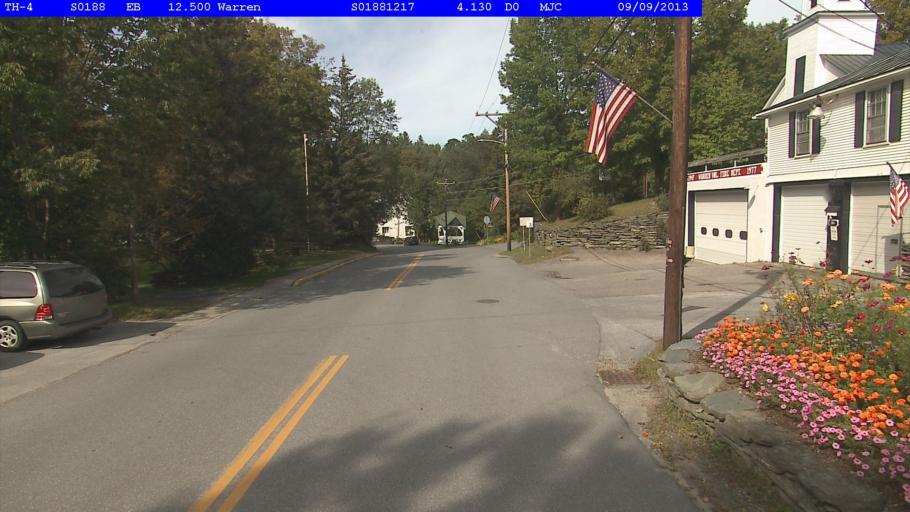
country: US
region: Vermont
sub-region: Washington County
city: Northfield
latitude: 44.1134
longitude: -72.8558
